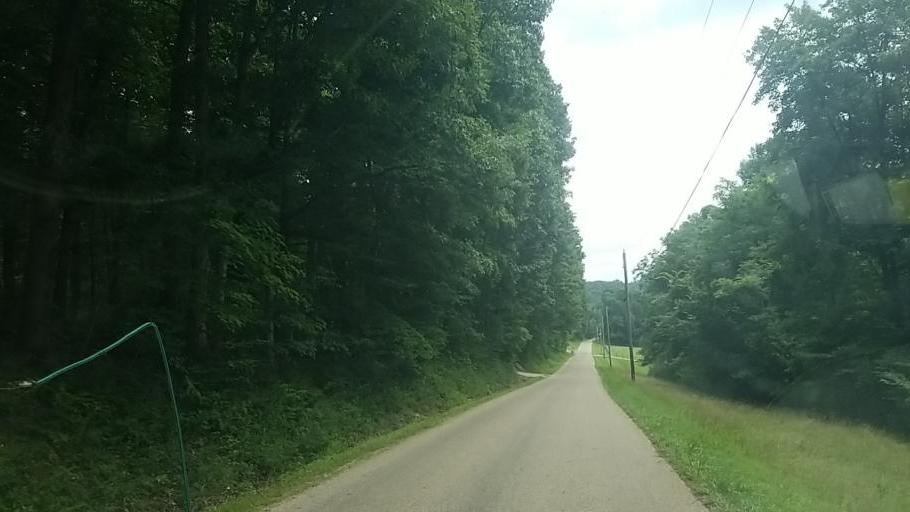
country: US
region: Ohio
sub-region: Knox County
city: Oak Hill
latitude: 40.2524
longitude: -82.2374
